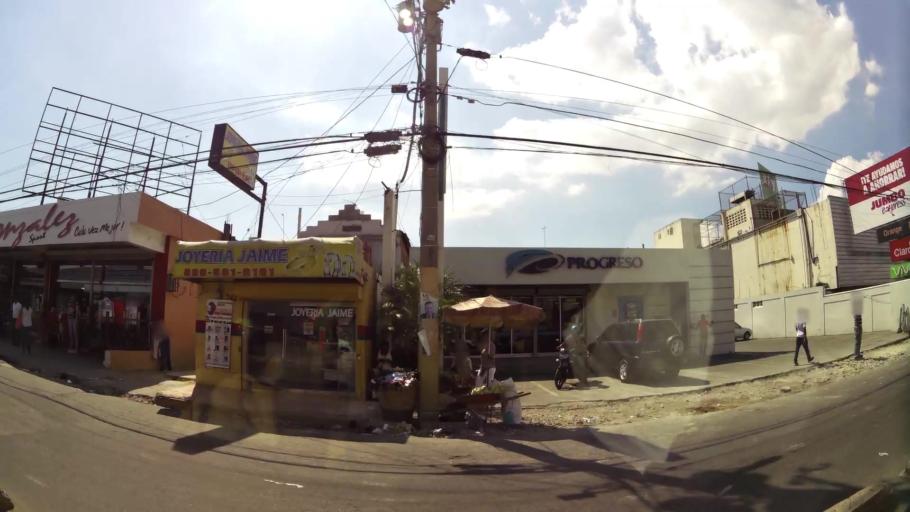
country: DO
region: Nacional
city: Santo Domingo
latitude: 18.4756
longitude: -69.9718
